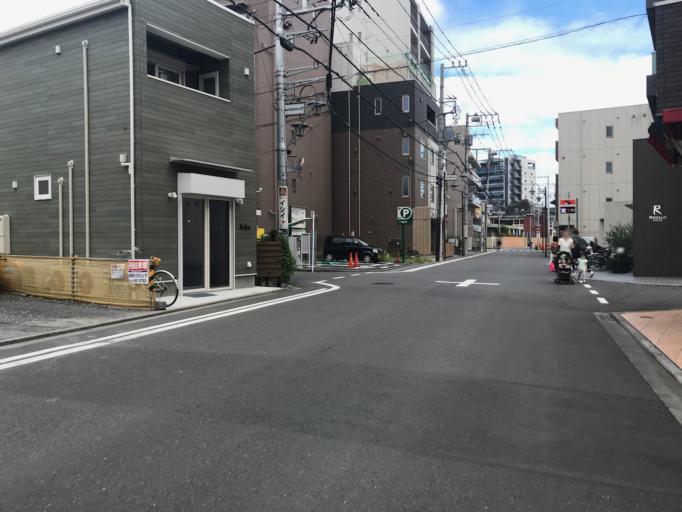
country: JP
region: Tokyo
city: Chofugaoka
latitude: 35.6199
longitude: 139.5641
